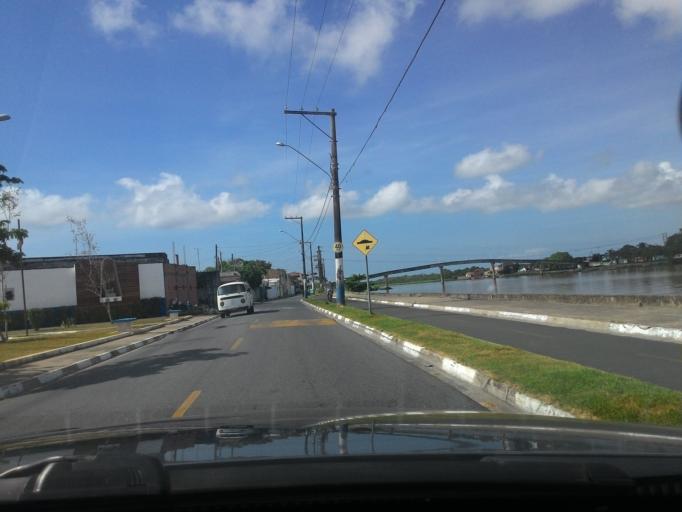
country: BR
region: Sao Paulo
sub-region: Iguape
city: Iguape
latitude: -24.7100
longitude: -47.5625
